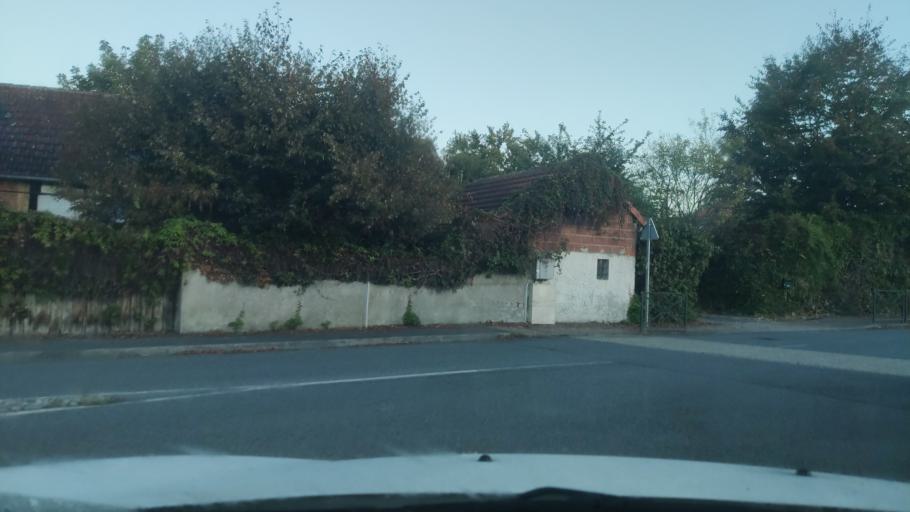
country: FR
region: Aquitaine
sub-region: Departement des Pyrenees-Atlantiques
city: Sauvagnon
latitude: 43.3983
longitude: -0.3856
